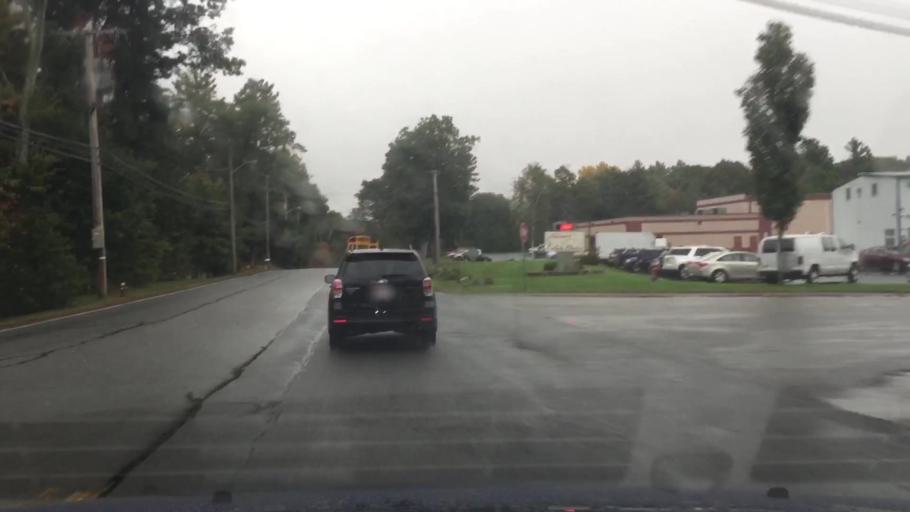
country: US
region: Massachusetts
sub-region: Middlesex County
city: Dracut
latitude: 42.6957
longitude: -71.2640
